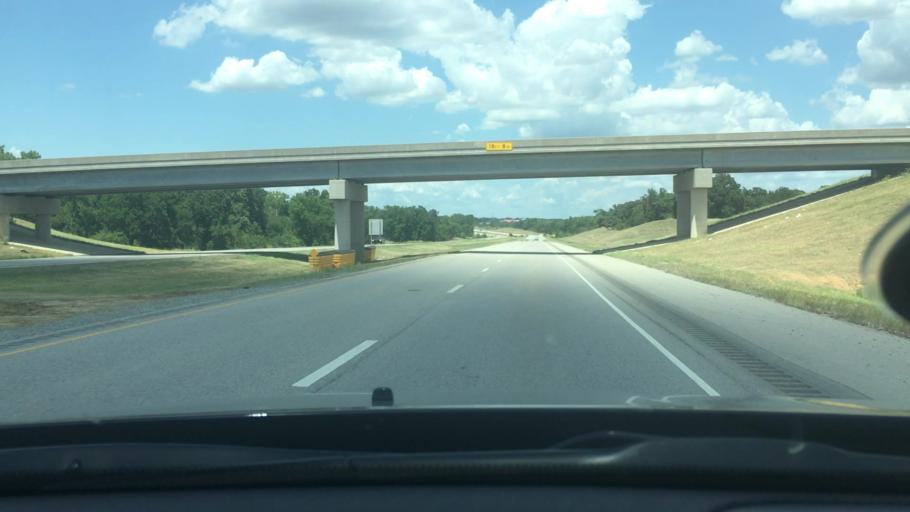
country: US
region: Oklahoma
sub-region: Bryan County
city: Calera
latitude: 33.9824
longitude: -96.4275
